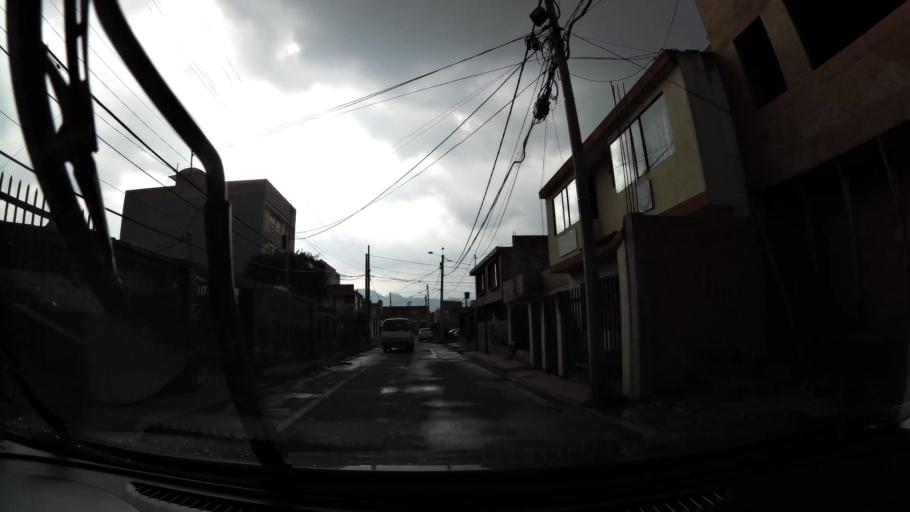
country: CO
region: Cundinamarca
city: Chia
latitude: 4.8611
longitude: -74.0484
